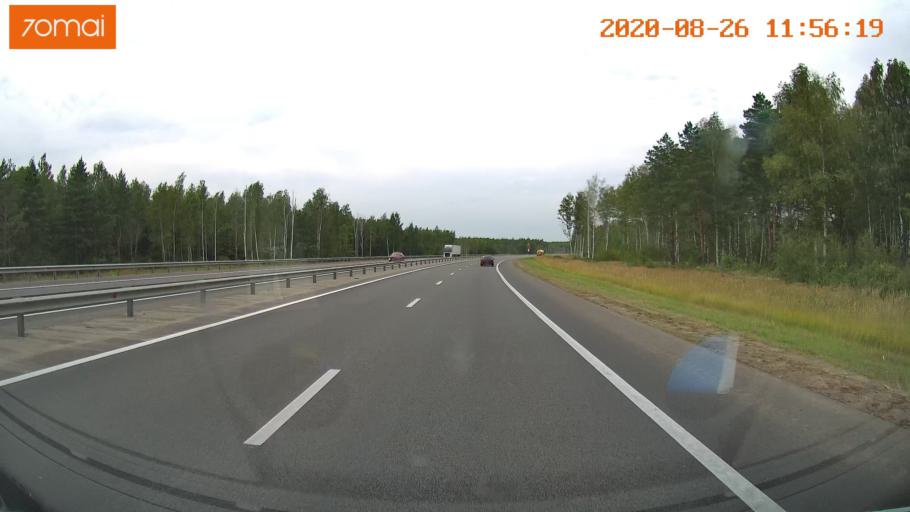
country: RU
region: Rjazan
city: Kiritsy
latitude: 54.2633
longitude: 40.3797
